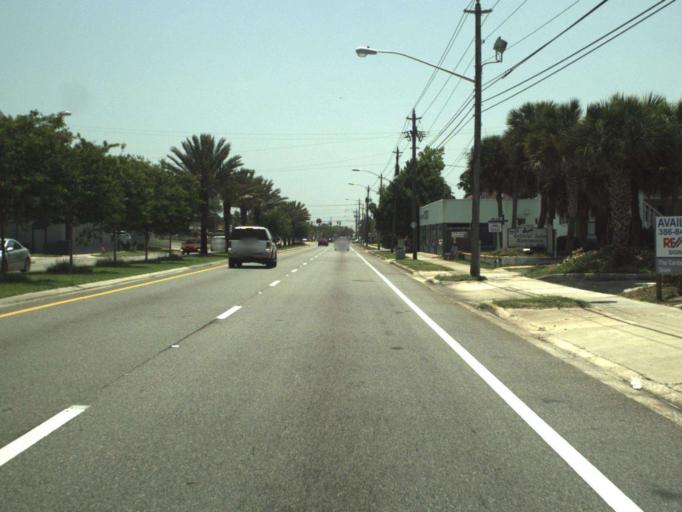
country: US
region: Florida
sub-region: Volusia County
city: Daytona Beach
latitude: 29.1913
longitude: -81.0124
